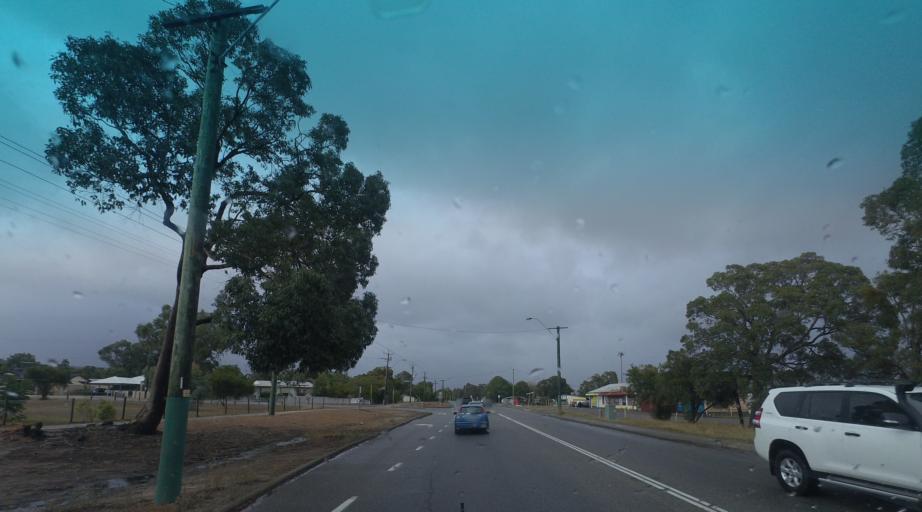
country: AU
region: Western Australia
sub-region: Serpentine-Jarrahdale
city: Byford
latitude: -32.2124
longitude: 116.0095
